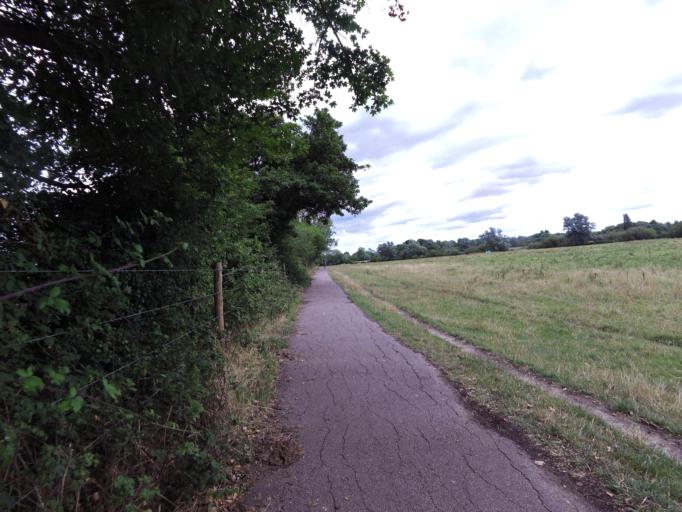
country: GB
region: England
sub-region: Cambridgeshire
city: Grantchester
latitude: 52.1888
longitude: 0.1023
